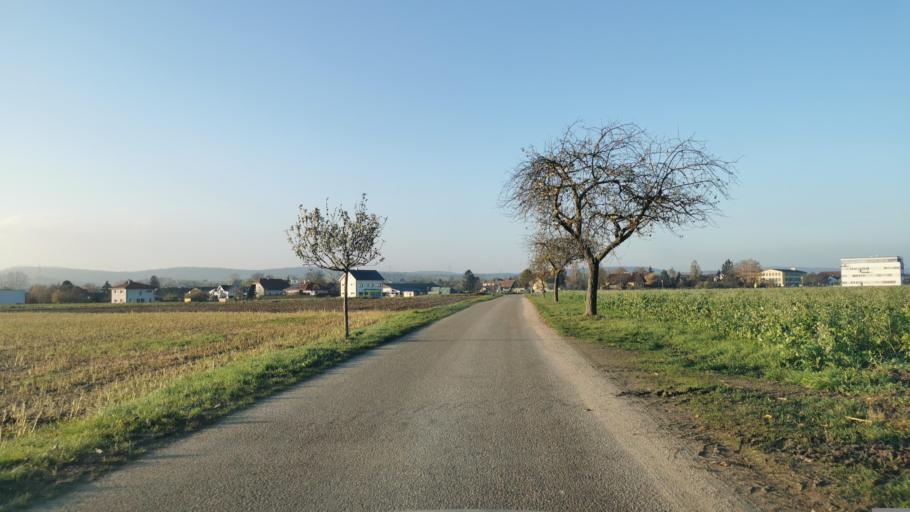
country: AT
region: Lower Austria
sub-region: Politischer Bezirk Korneuburg
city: Harmannsdorf
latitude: 48.3860
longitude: 16.3771
